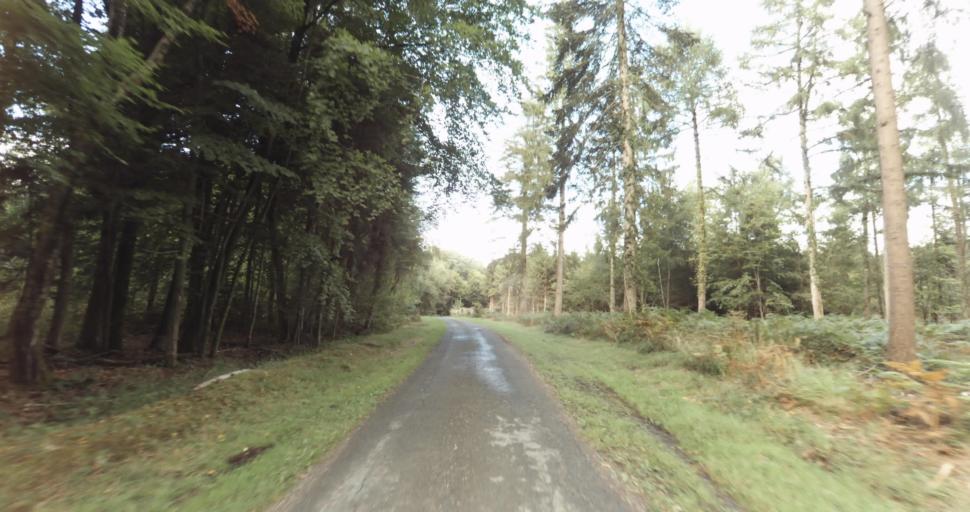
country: FR
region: Lower Normandy
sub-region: Departement de l'Orne
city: Sainte-Gauburge-Sainte-Colombe
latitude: 48.7554
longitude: 0.4144
